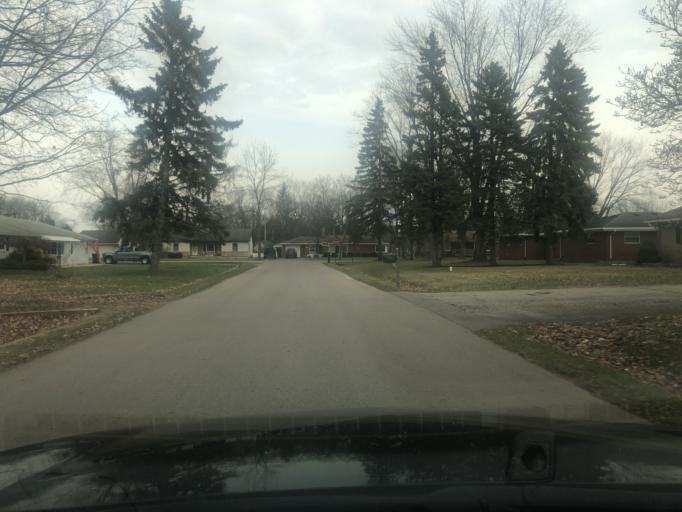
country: US
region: Michigan
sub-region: Wayne County
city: Belleville
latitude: 42.2177
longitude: -83.4823
